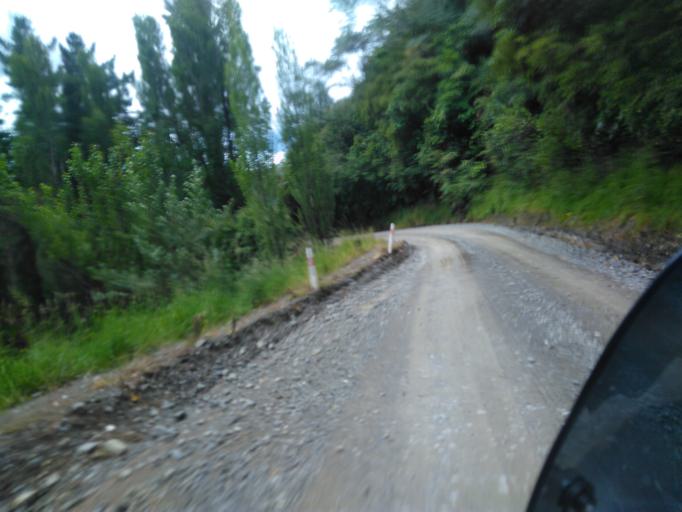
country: NZ
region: Gisborne
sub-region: Gisborne District
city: Gisborne
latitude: -38.0529
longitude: 178.1086
